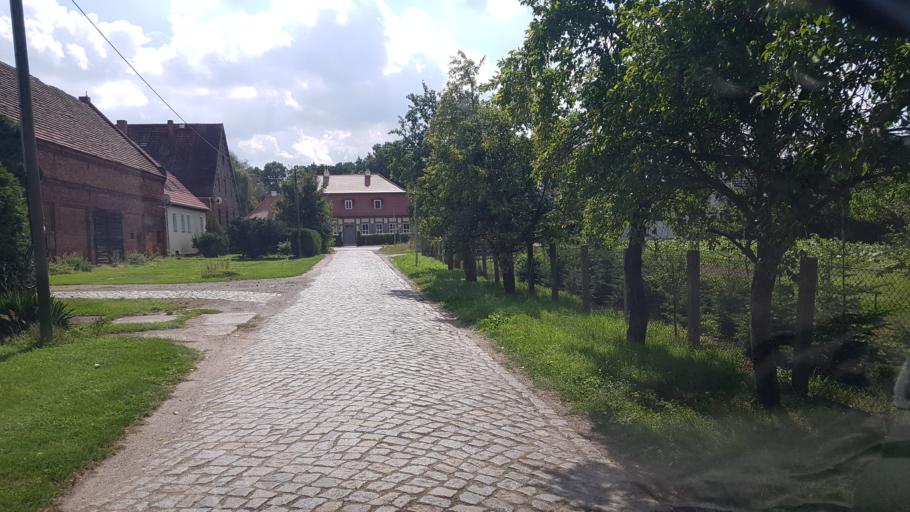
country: DE
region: Brandenburg
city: Lubbenau
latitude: 51.8496
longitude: 13.9029
